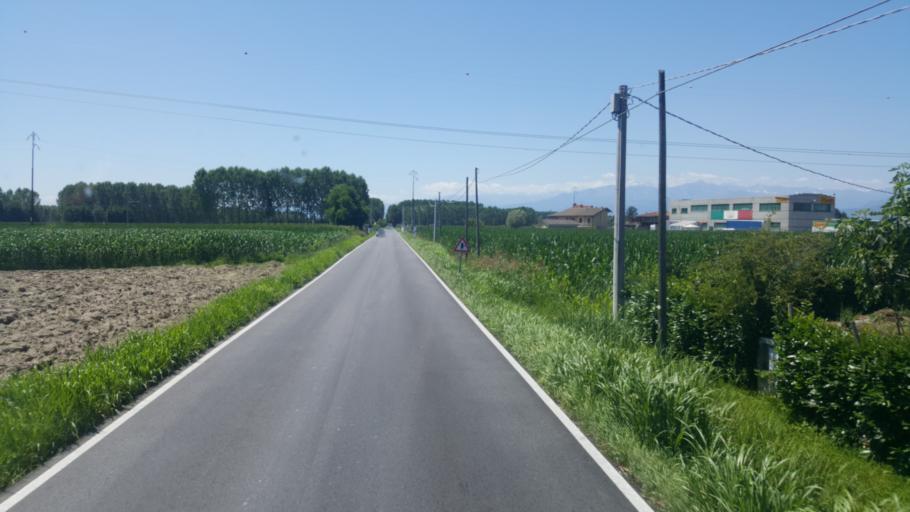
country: IT
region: Piedmont
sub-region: Provincia di Torino
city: Volvera
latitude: 44.9344
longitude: 7.5029
